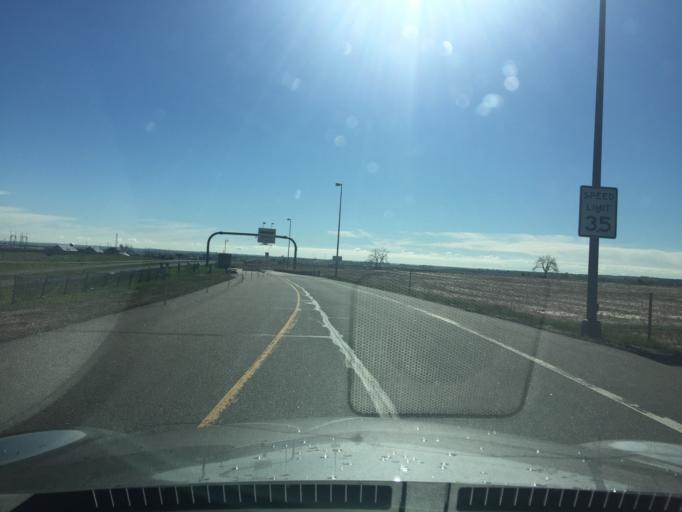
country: US
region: Colorado
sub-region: Boulder County
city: Lafayette
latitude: 39.9833
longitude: -105.0176
